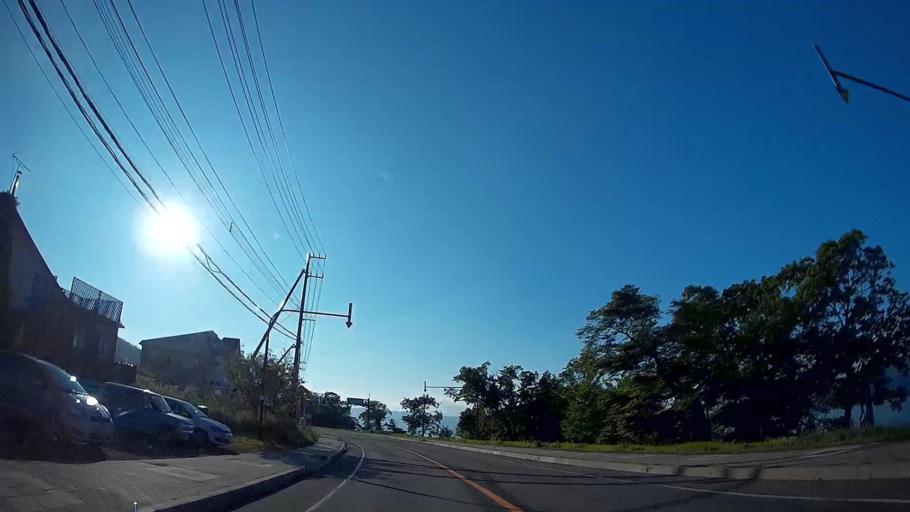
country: JP
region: Hokkaido
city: Date
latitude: 42.5594
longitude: 140.8533
